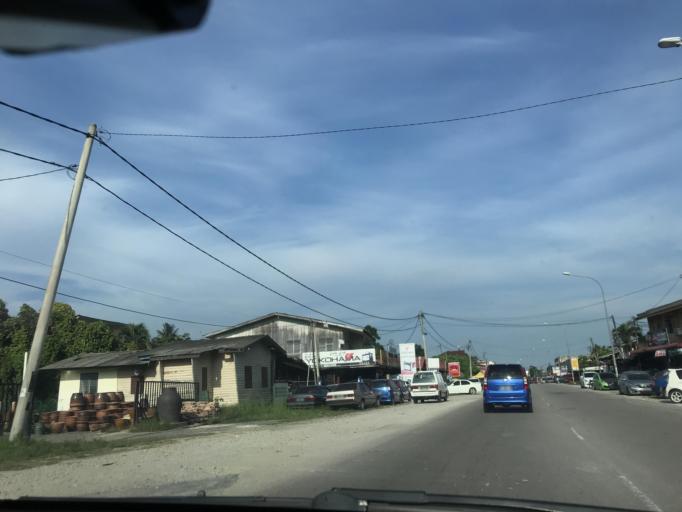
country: MY
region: Kelantan
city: Kota Bharu
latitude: 6.1234
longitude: 102.2798
